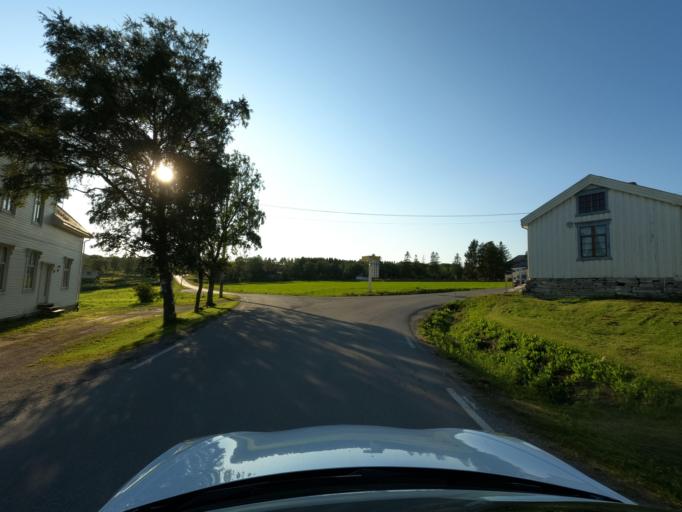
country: NO
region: Nordland
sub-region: Ballangen
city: Ballangen
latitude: 68.4586
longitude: 16.6998
